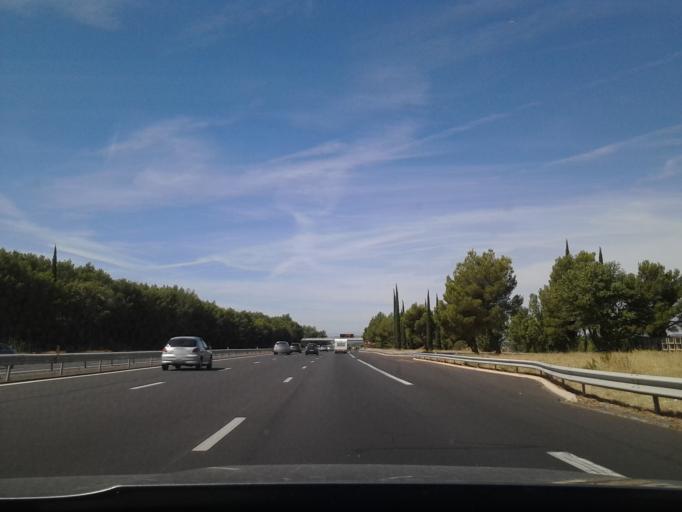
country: FR
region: Languedoc-Roussillon
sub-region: Departement de l'Aude
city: Vinassan
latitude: 43.1919
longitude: 3.0691
